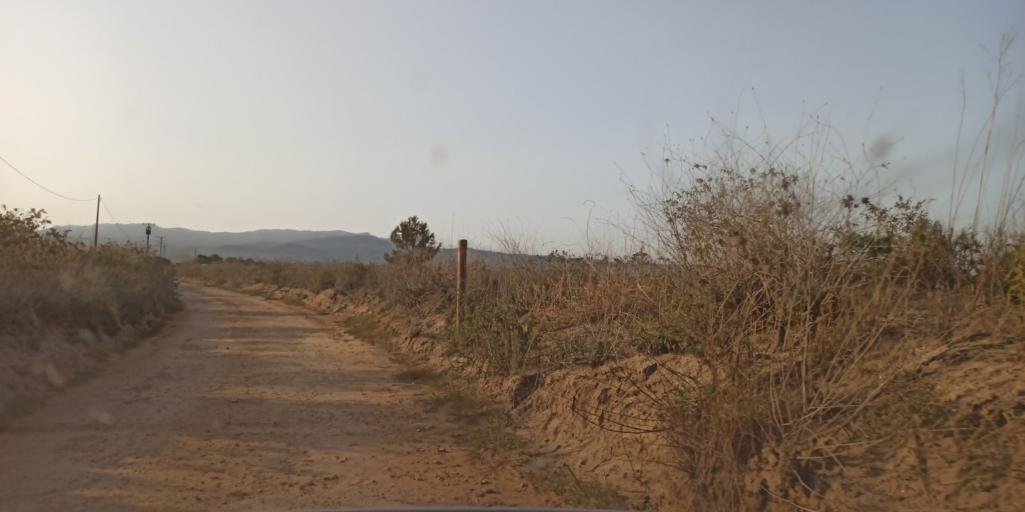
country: ES
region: Catalonia
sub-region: Provincia de Tarragona
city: L'Ampolla
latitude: 40.7836
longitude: 0.7121
